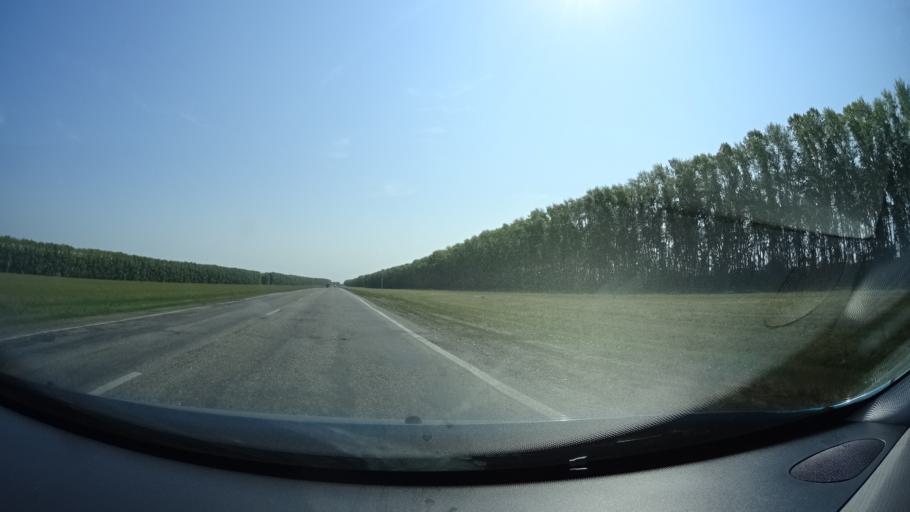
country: RU
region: Bashkortostan
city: Karmaskaly
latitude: 54.3974
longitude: 56.1027
